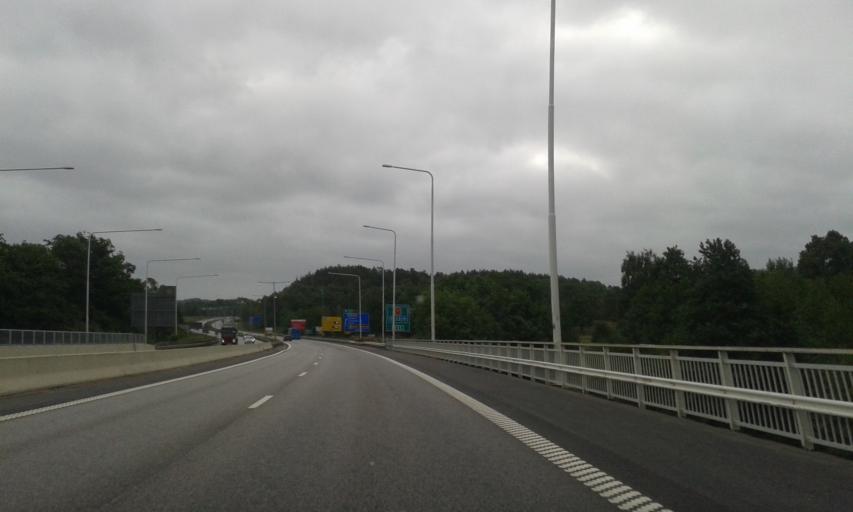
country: SE
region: Vaestra Goetaland
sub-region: Kungalvs Kommun
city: Kungalv
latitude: 57.8626
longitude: 11.9763
